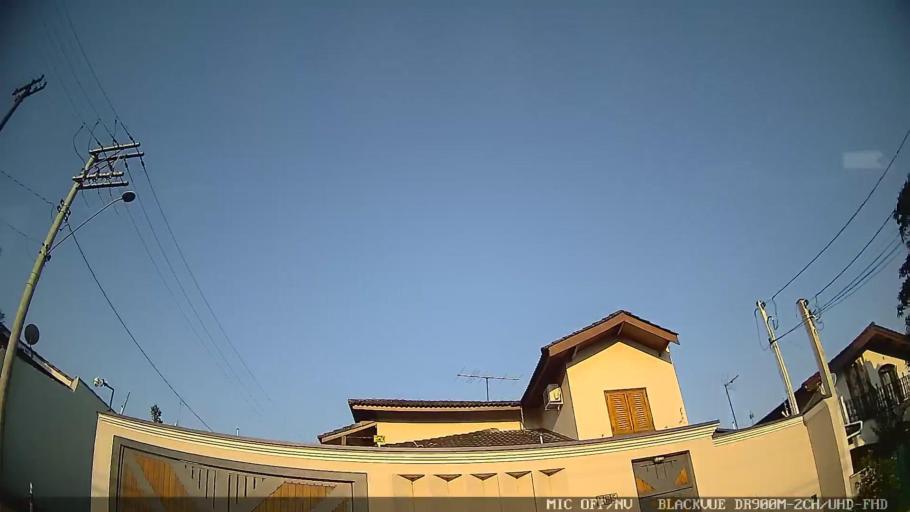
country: BR
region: Sao Paulo
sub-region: Itatiba
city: Itatiba
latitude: -23.0027
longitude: -46.8229
